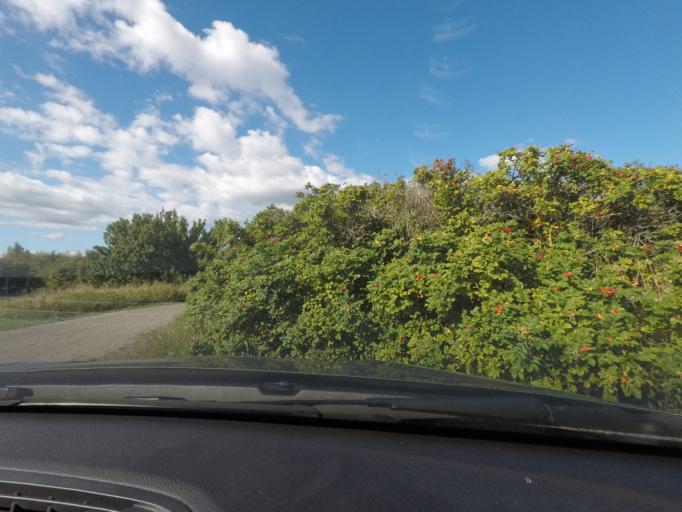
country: DK
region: Zealand
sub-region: Guldborgsund Kommune
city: Sakskobing
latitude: 54.9684
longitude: 11.5604
